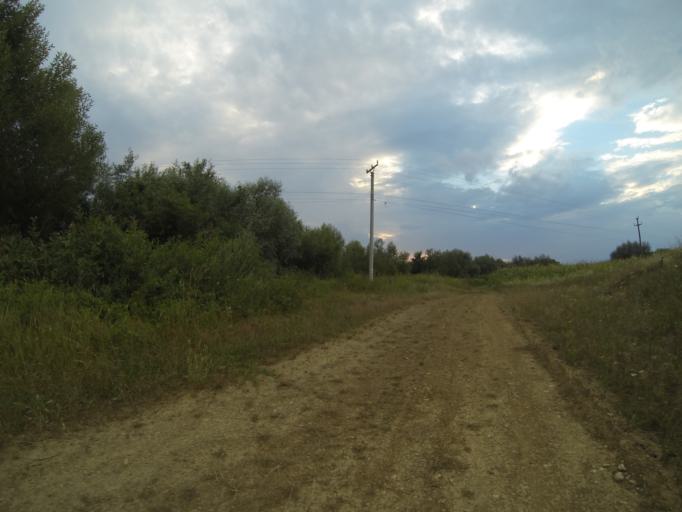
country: RO
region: Brasov
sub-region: Comuna Sinca Veche
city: Sinca Veche
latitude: 45.7729
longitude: 25.1647
